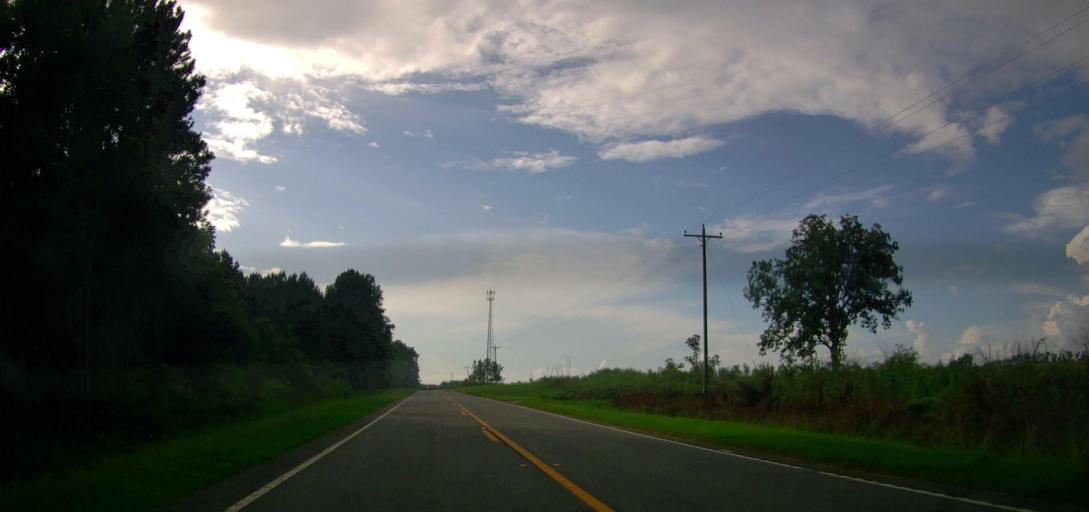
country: US
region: Georgia
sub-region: Coffee County
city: Nicholls
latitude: 31.3256
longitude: -82.5804
